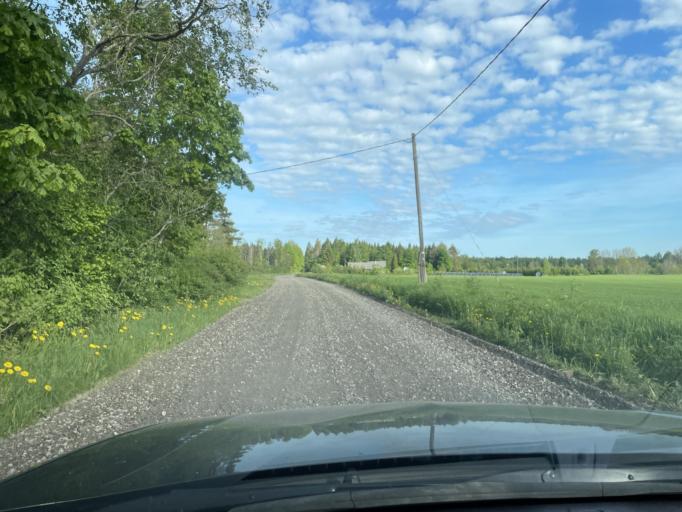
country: EE
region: Harju
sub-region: Keila linn
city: Keila
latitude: 59.2999
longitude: 24.3118
